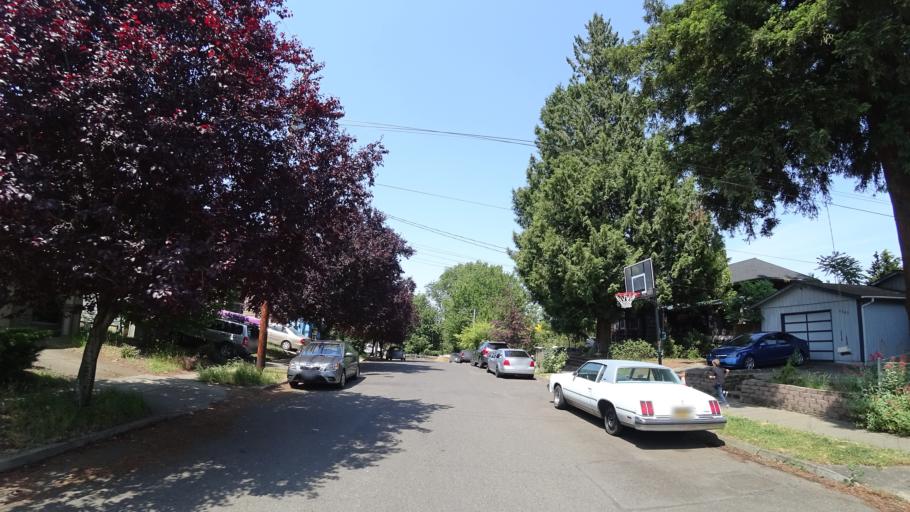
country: US
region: Washington
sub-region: Clark County
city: Vancouver
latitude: 45.5865
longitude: -122.6951
